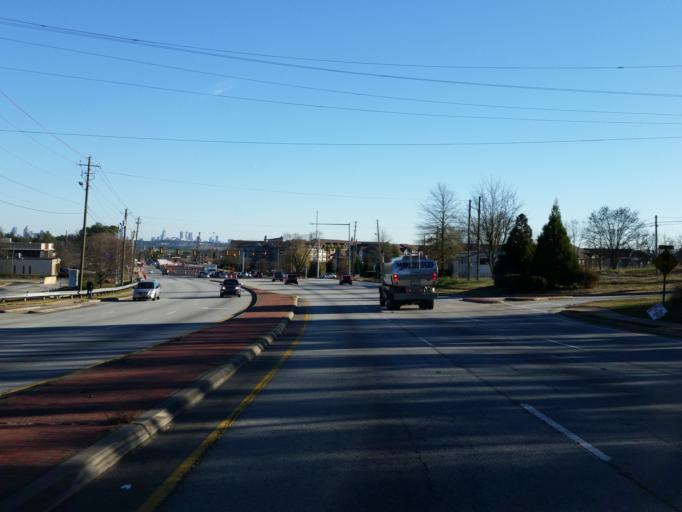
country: US
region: Georgia
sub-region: Cobb County
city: Vinings
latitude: 33.8467
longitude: -84.4920
